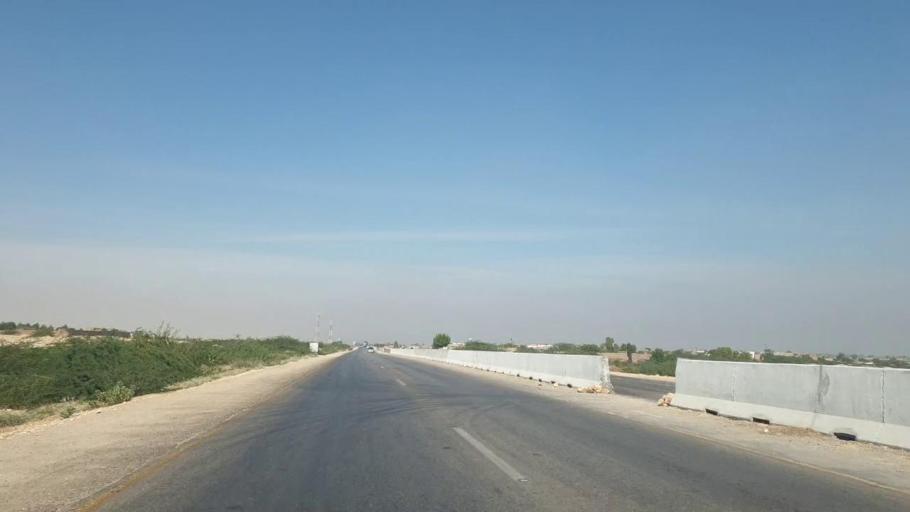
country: PK
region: Sindh
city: Hala
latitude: 25.6936
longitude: 68.2955
